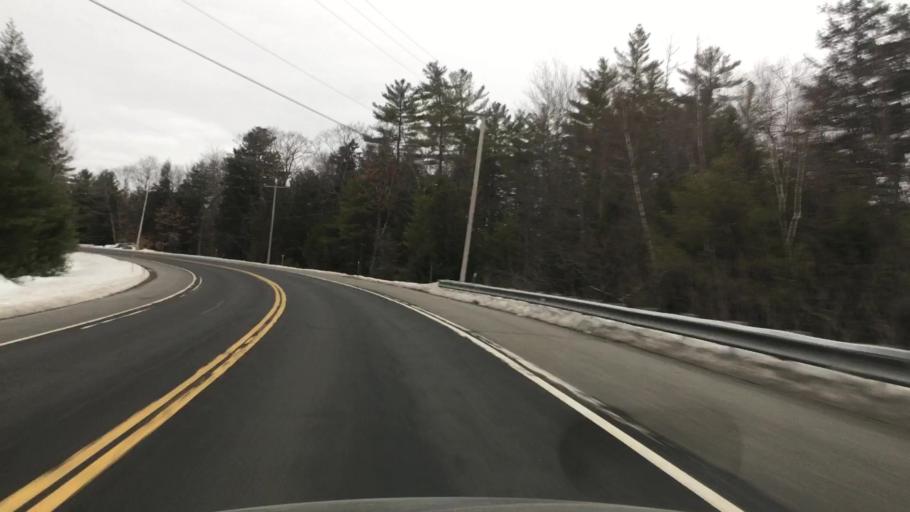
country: US
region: New Hampshire
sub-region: Merrimack County
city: Henniker
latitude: 43.2168
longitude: -71.8724
